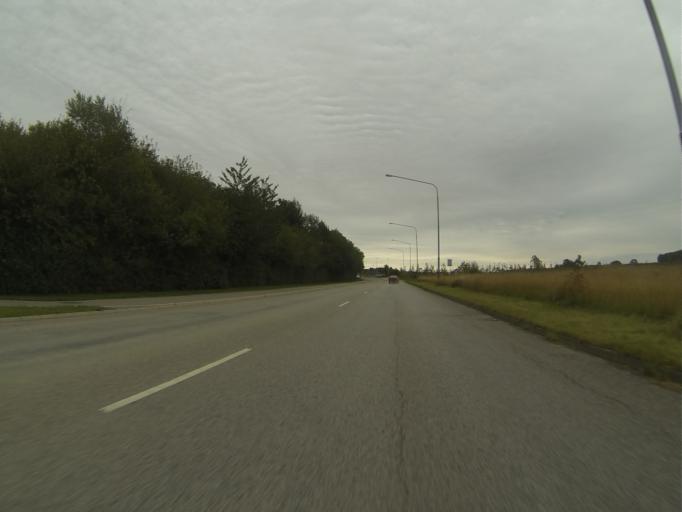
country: SE
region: Skane
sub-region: Staffanstorps Kommun
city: Staffanstorp
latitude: 55.6316
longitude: 13.1935
